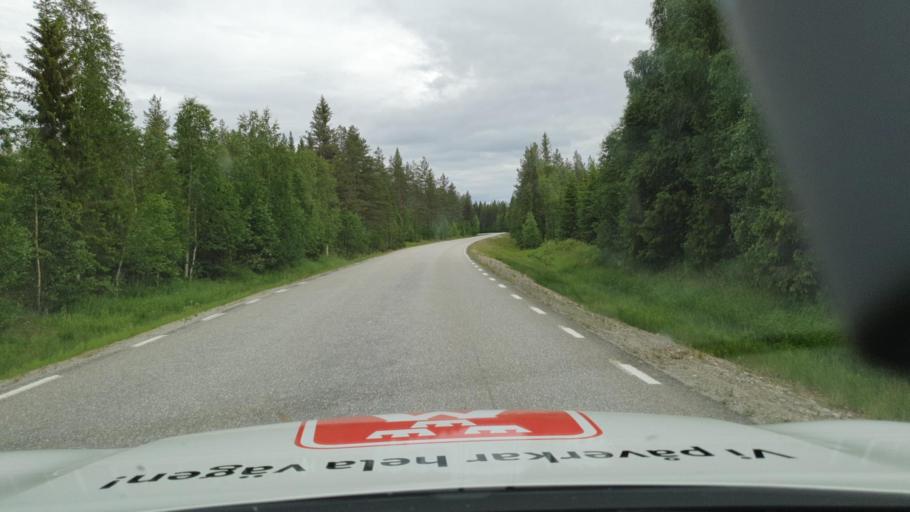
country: SE
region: Vaesterbotten
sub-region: Lycksele Kommun
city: Soderfors
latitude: 64.3359
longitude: 18.1429
